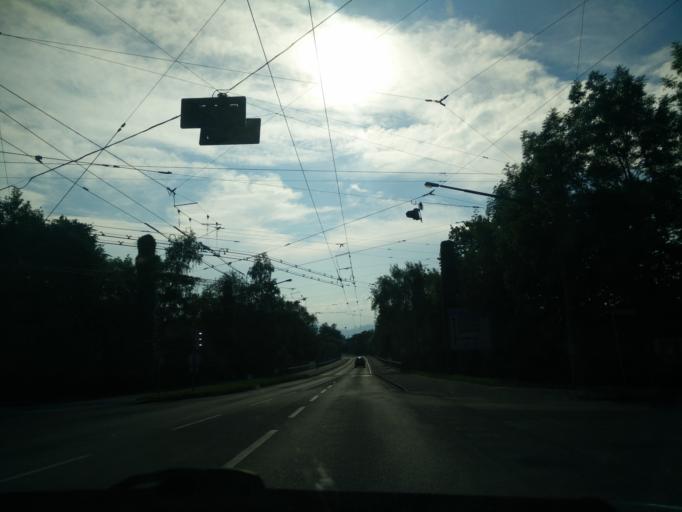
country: AT
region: Salzburg
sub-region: Politischer Bezirk Salzburg-Umgebung
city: Elsbethen
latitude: 47.7708
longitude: 13.0770
